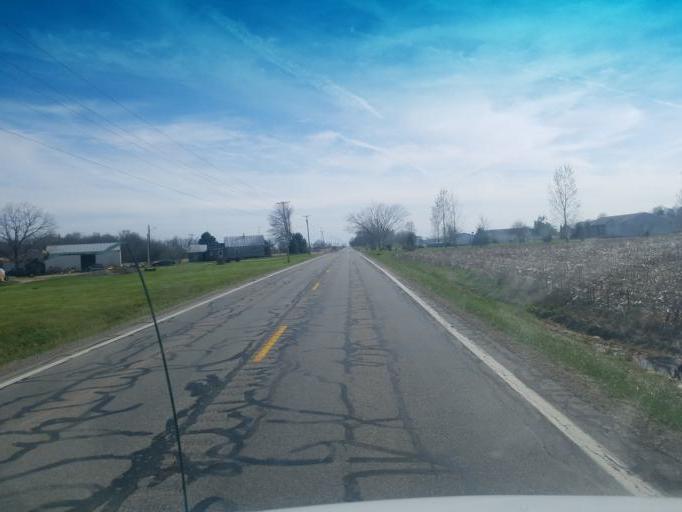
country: US
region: Ohio
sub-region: Marion County
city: Prospect
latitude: 40.4615
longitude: -83.2120
